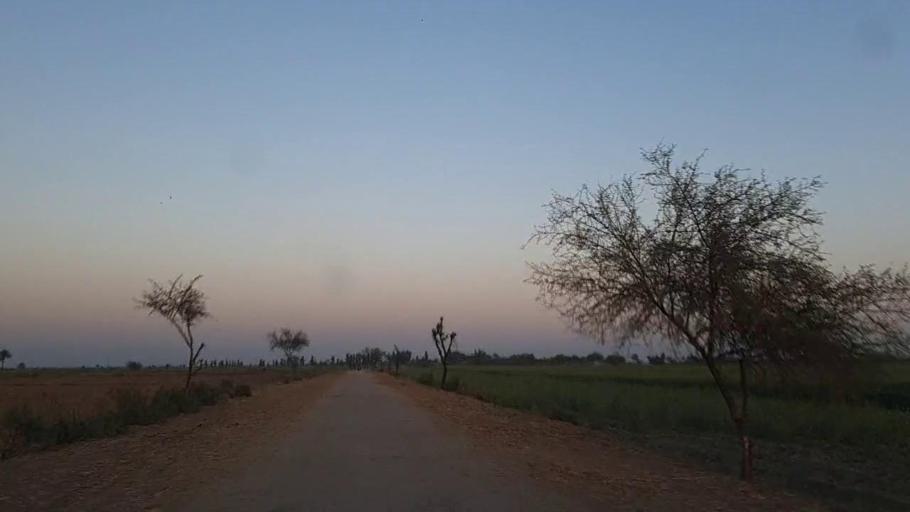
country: PK
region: Sindh
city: Samaro
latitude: 25.3105
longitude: 69.4070
